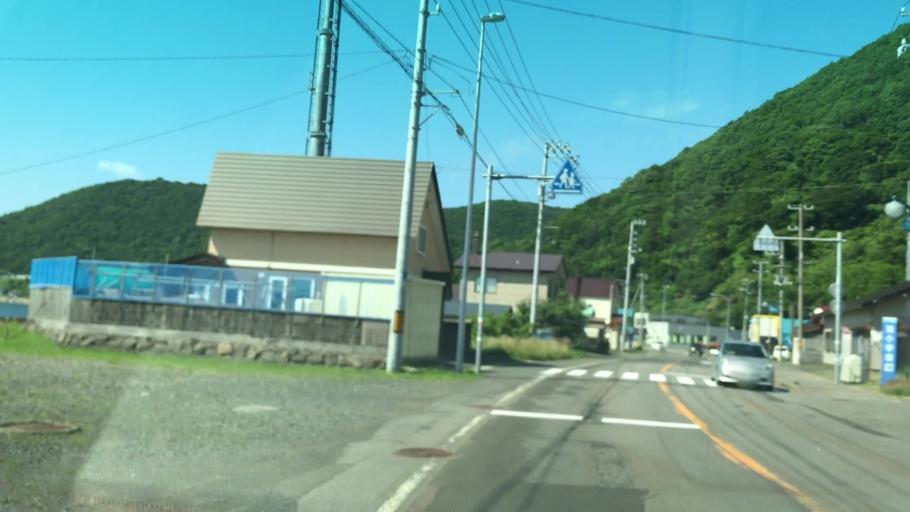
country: JP
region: Hokkaido
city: Iwanai
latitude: 43.0994
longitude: 140.4609
